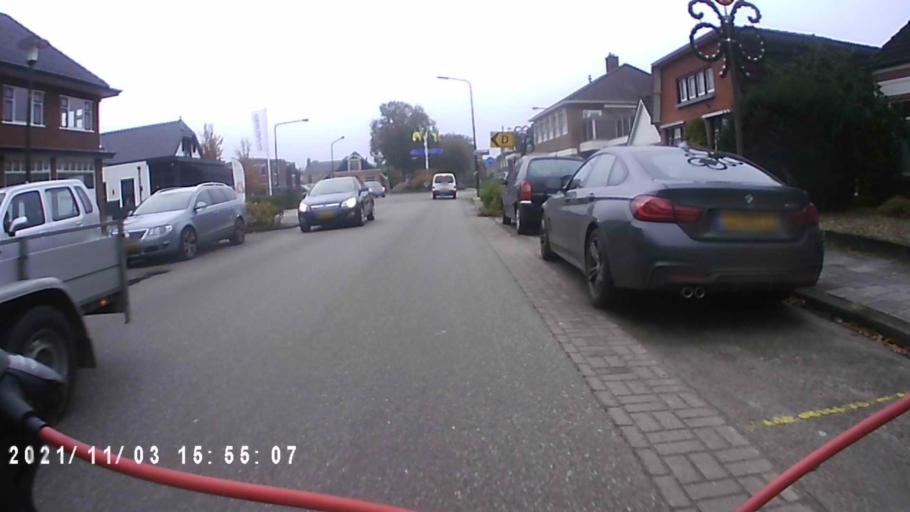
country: NL
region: Groningen
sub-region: Gemeente Leek
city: Leek
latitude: 53.0659
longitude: 6.3315
